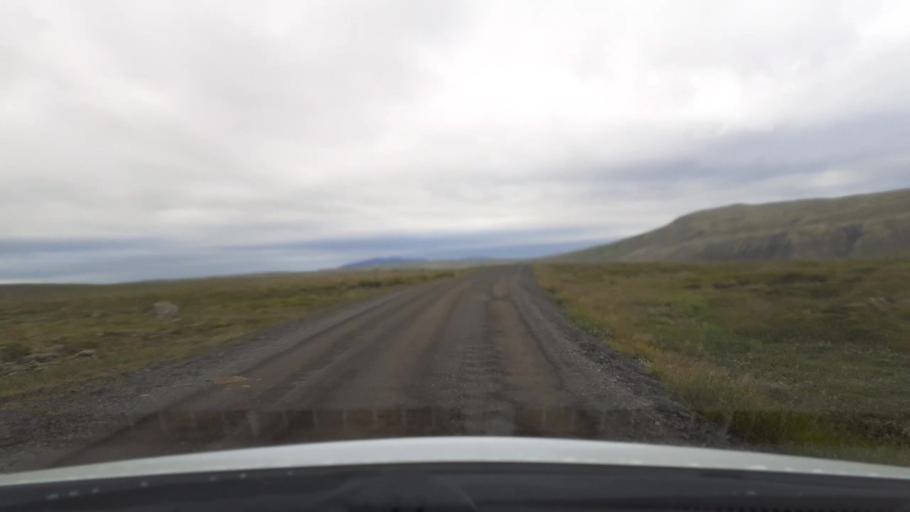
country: IS
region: Capital Region
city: Mosfellsbaer
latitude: 64.1934
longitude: -21.5430
